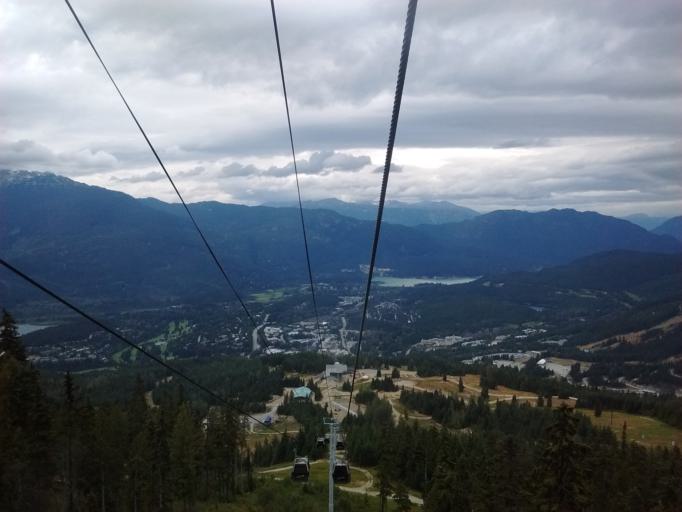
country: CA
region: British Columbia
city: Whistler
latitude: 50.0909
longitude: -122.9502
